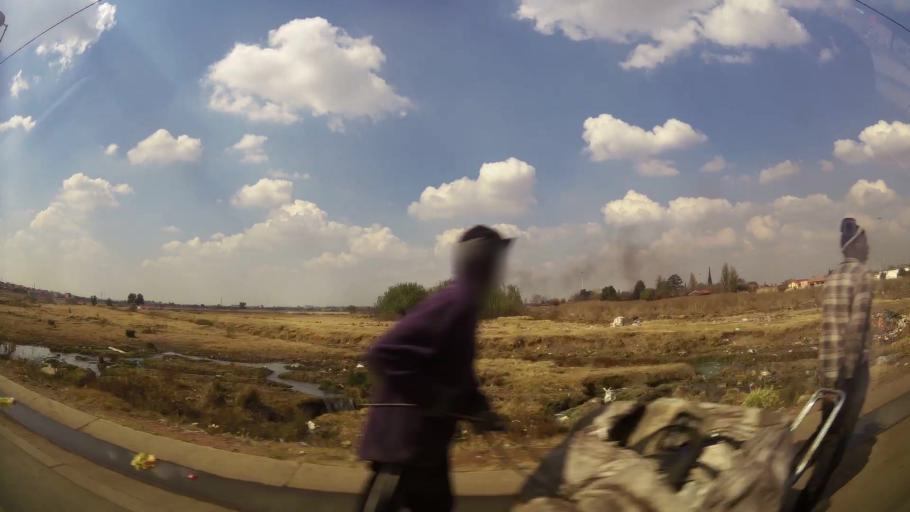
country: ZA
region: Gauteng
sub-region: Ekurhuleni Metropolitan Municipality
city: Germiston
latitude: -26.3020
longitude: 28.1507
